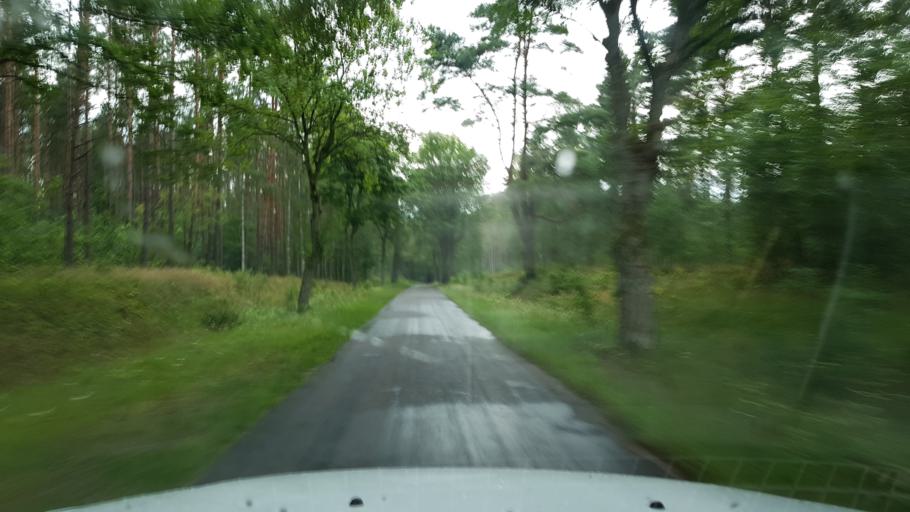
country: PL
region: West Pomeranian Voivodeship
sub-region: Powiat szczecinecki
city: Bialy Bor
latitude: 53.8747
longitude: 16.7009
